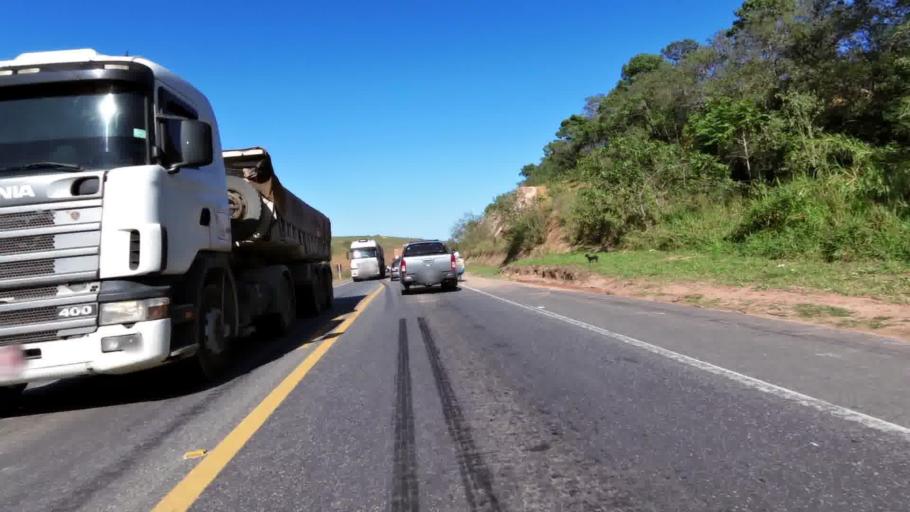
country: BR
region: Espirito Santo
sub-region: Alfredo Chaves
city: Alfredo Chaves
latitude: -20.7158
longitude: -40.7291
